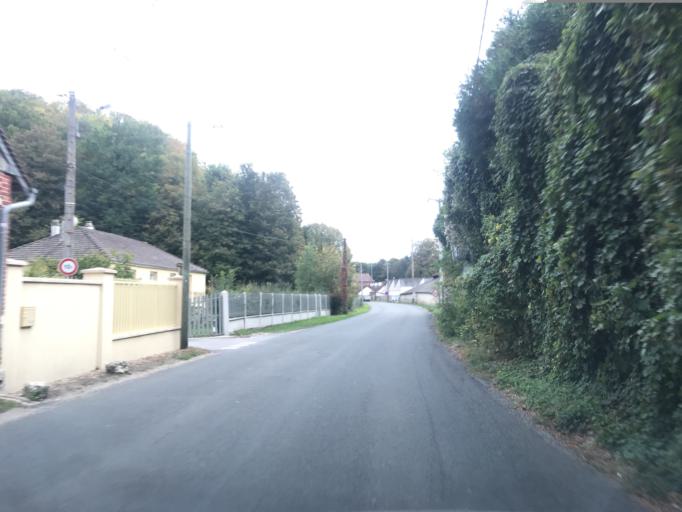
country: FR
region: Haute-Normandie
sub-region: Departement de l'Eure
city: Acquigny
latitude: 49.1674
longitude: 1.1915
